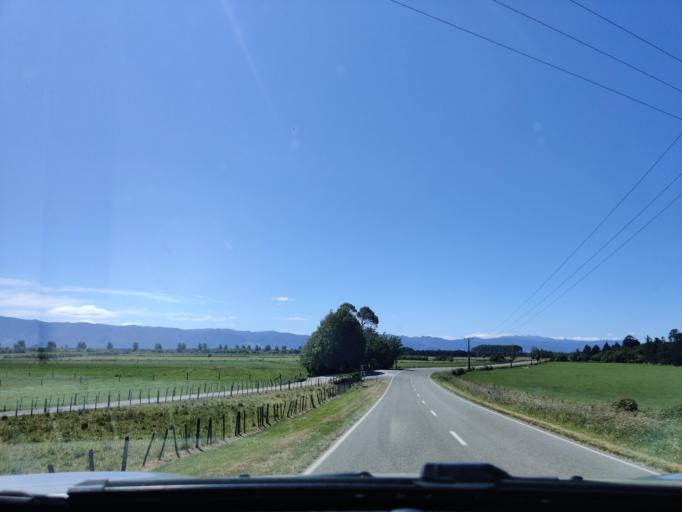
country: NZ
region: Wellington
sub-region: South Wairarapa District
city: Waipawa
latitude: -41.3007
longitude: 175.2706
